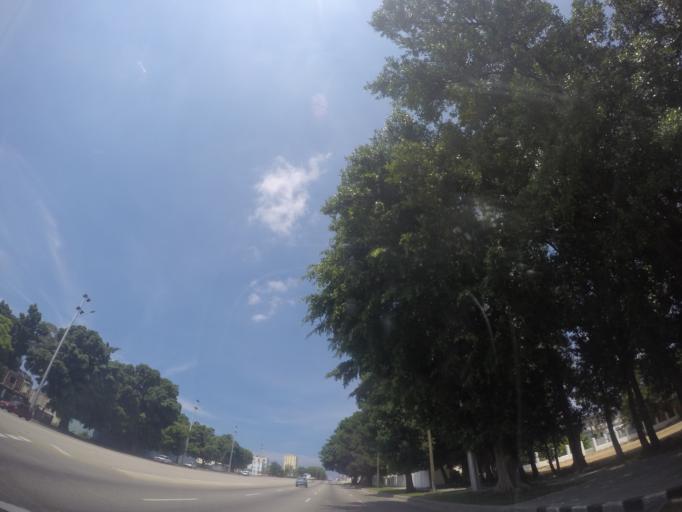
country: CU
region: La Habana
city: Havana
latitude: 23.1273
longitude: -82.3905
